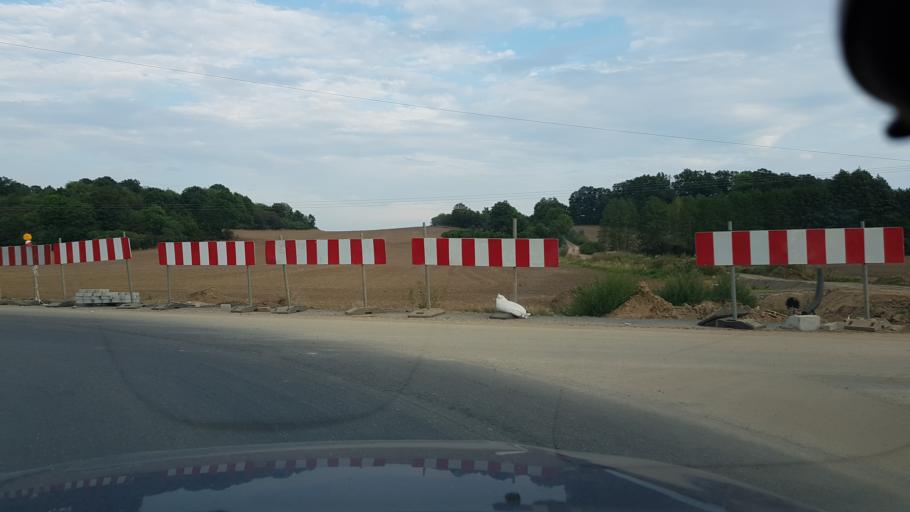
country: PL
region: Lower Silesian Voivodeship
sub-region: Powiat jaworski
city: Bolkow
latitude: 50.9147
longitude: 16.1134
